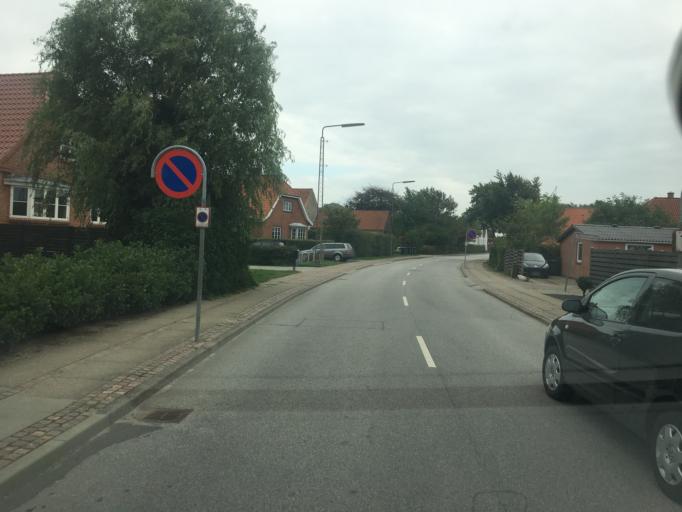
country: DK
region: South Denmark
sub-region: Tonder Kommune
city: Tonder
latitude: 54.9372
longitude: 8.8568
